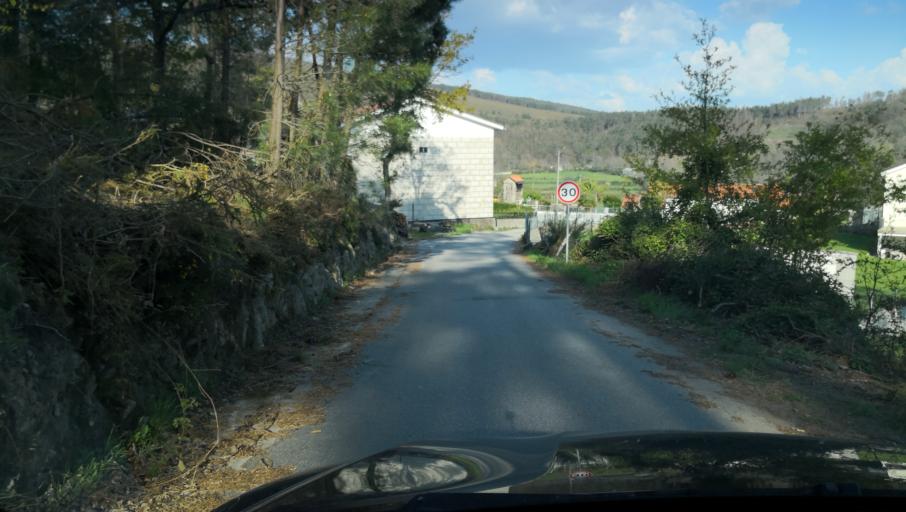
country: PT
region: Vila Real
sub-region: Vila Real
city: Vila Real
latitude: 41.3144
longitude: -7.8624
